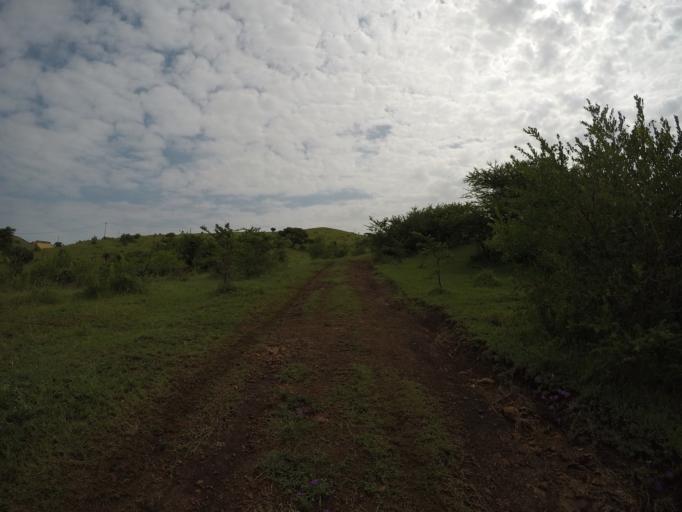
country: ZA
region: KwaZulu-Natal
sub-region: uThungulu District Municipality
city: Empangeni
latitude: -28.6219
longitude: 31.8949
